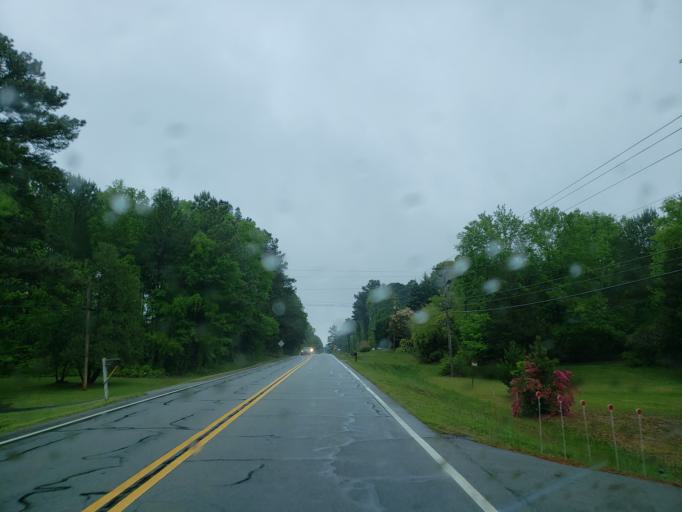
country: US
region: Georgia
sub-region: Paulding County
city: Dallas
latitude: 33.8426
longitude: -84.8624
